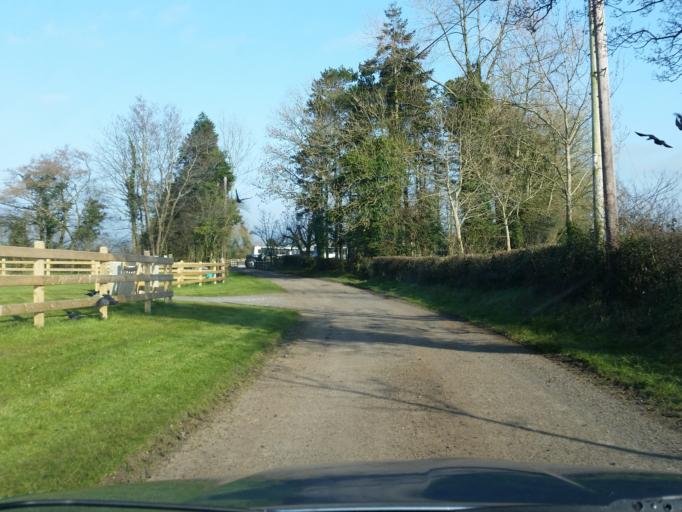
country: IE
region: Ulster
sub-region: County Monaghan
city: Clones
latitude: 54.2255
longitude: -7.2411
